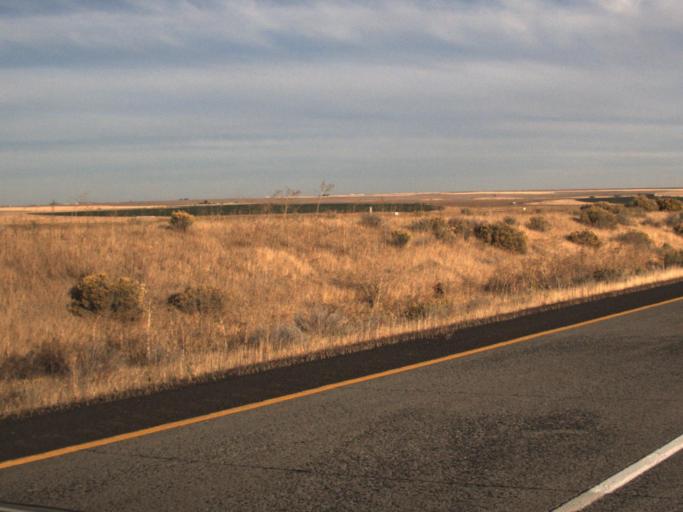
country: US
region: Washington
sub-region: Franklin County
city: Connell
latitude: 46.6971
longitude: -118.8364
